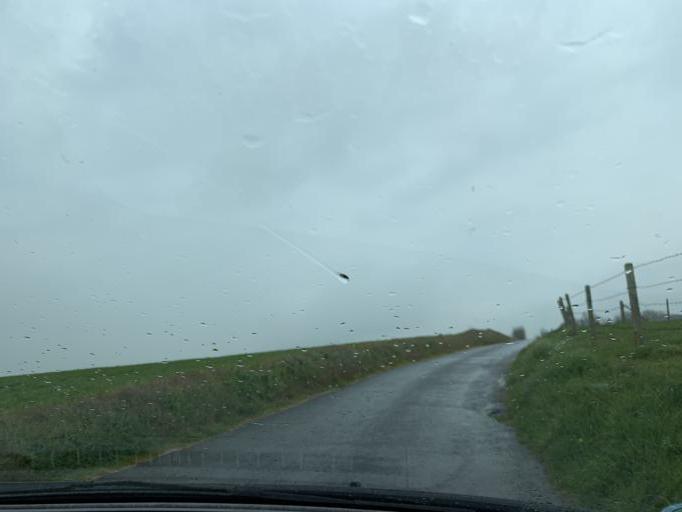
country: FR
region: Haute-Normandie
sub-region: Departement de la Seine-Maritime
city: Saint-Jouin-Bruneval
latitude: 49.6800
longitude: 0.1691
